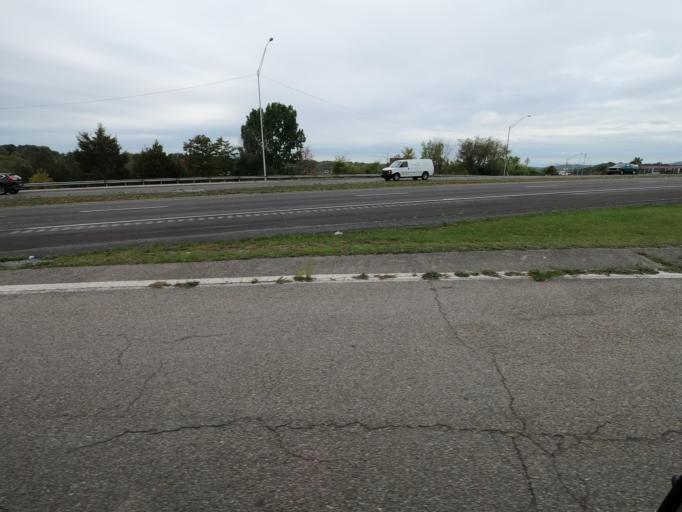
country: US
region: Tennessee
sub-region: Sullivan County
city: Bloomingdale
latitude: 36.5437
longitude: -82.5080
